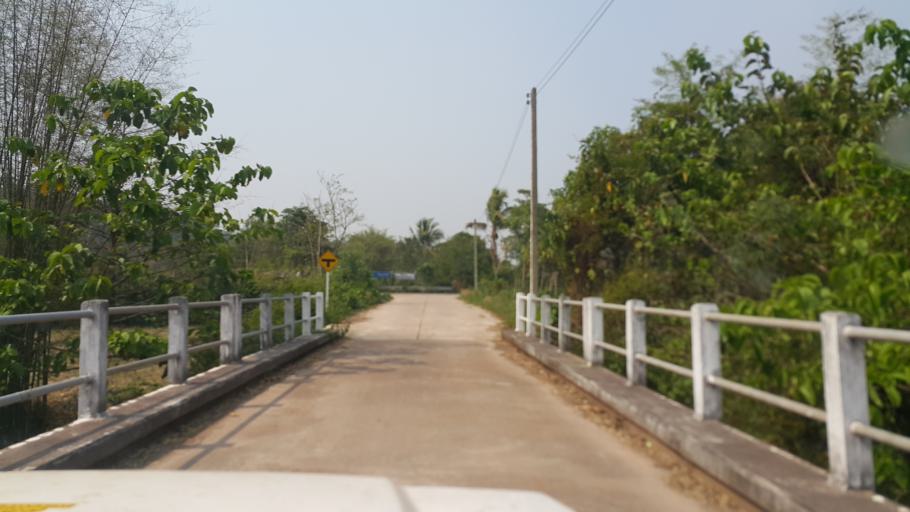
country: TH
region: Nakhon Phanom
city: Ban Phaeng
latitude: 17.9856
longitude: 104.1451
